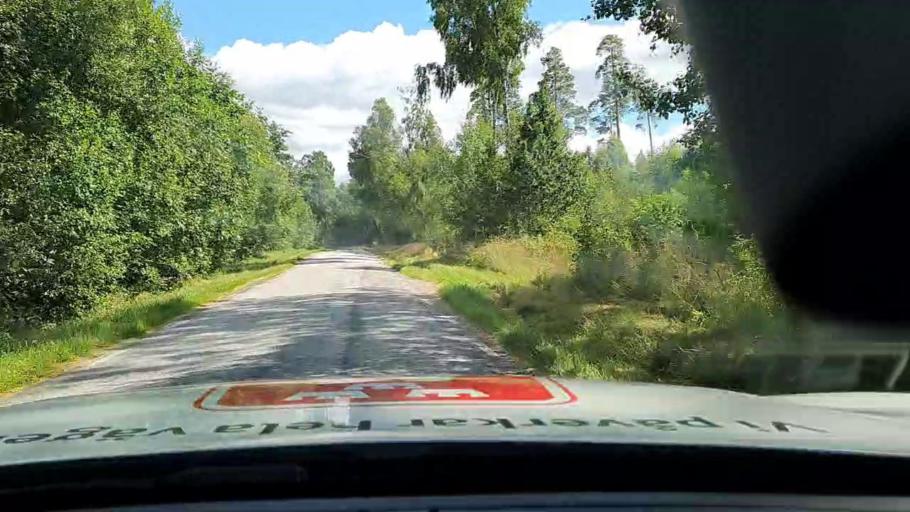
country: SE
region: Vaestra Goetaland
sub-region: Toreboda Kommun
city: Toereboda
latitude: 58.5706
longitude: 14.1281
